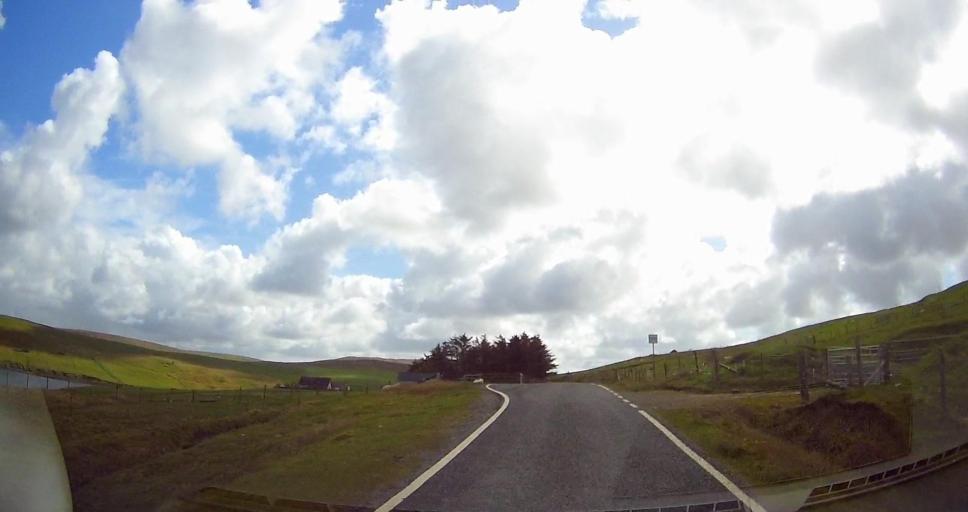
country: GB
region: Scotland
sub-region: Shetland Islands
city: Lerwick
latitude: 60.5334
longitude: -1.3611
